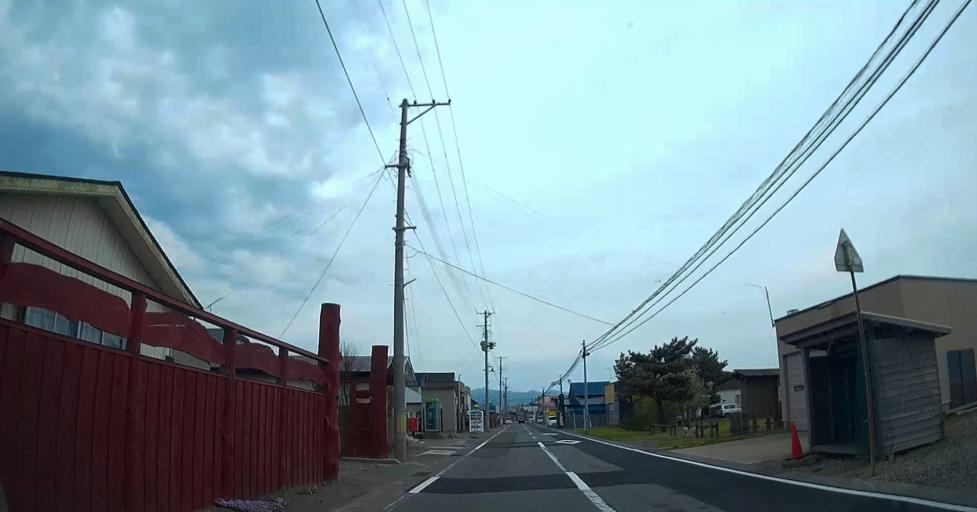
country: JP
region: Aomori
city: Shimokizukuri
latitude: 41.0311
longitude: 140.3269
